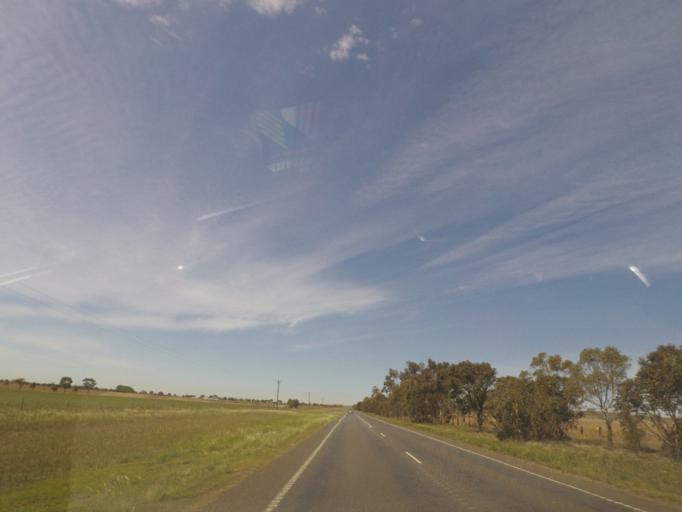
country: AU
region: Victoria
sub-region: Moorabool
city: Bacchus Marsh
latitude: -37.7582
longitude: 144.4414
